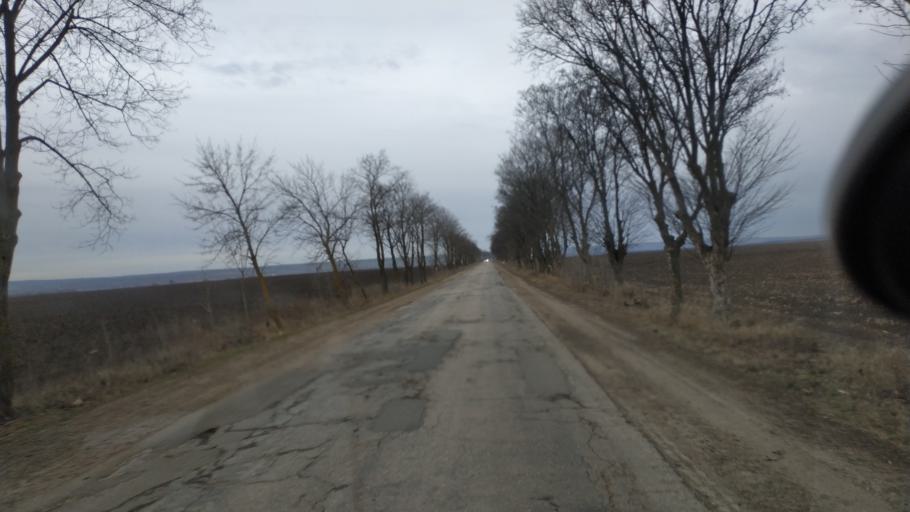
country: MD
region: Telenesti
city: Cocieri
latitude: 47.2661
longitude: 29.0967
